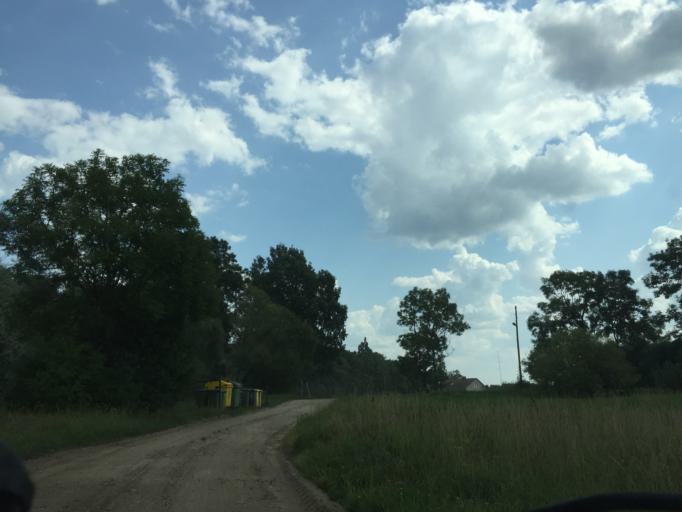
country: LT
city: Naujoji Akmene
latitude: 56.3439
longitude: 23.0540
